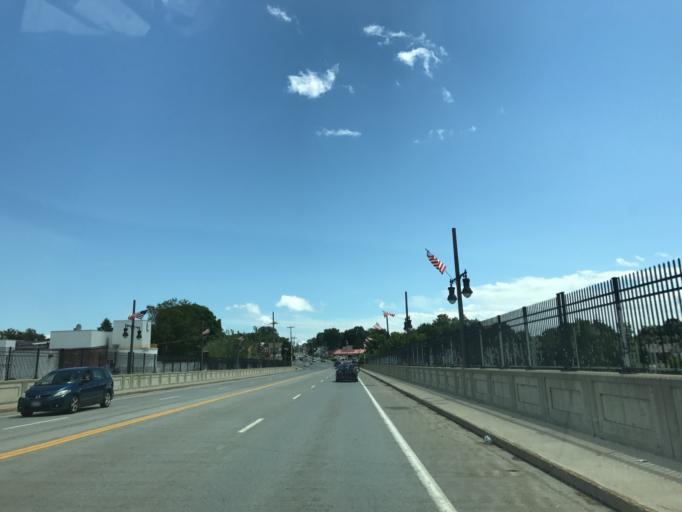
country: US
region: New York
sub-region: Warren County
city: Glens Falls
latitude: 43.3064
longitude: -73.6416
